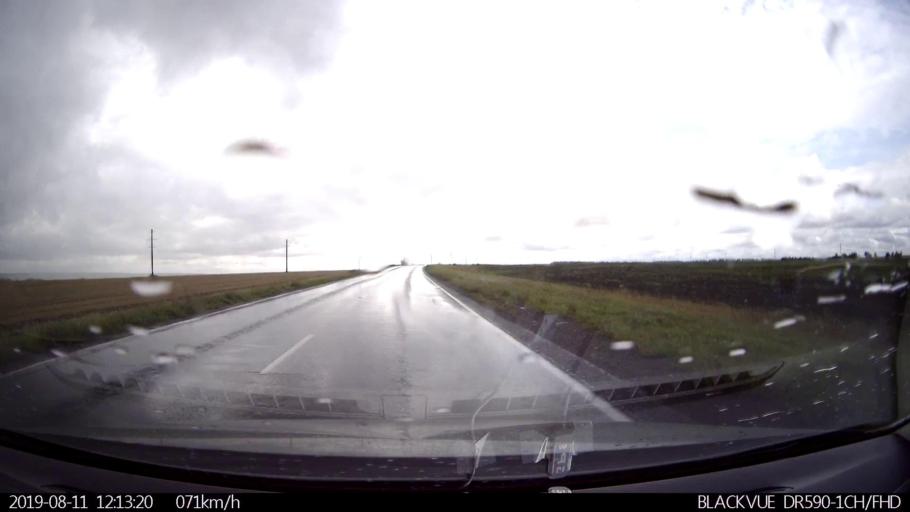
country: RU
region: Ulyanovsk
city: Silikatnyy
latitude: 53.9629
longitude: 47.9928
